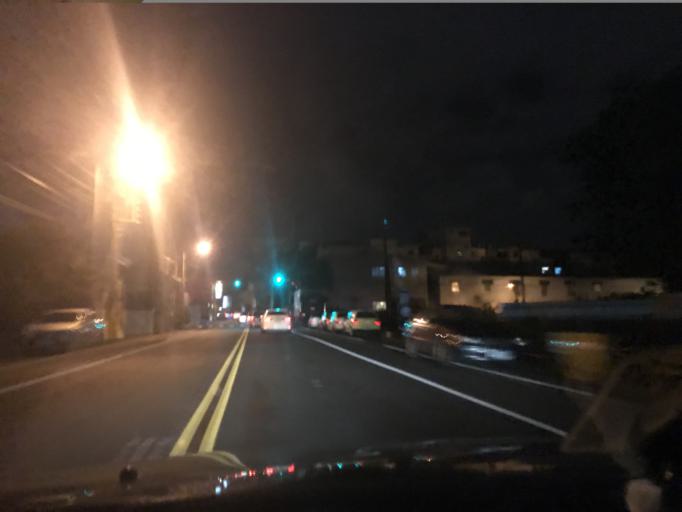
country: TW
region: Taiwan
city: Daxi
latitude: 24.9416
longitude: 121.2429
